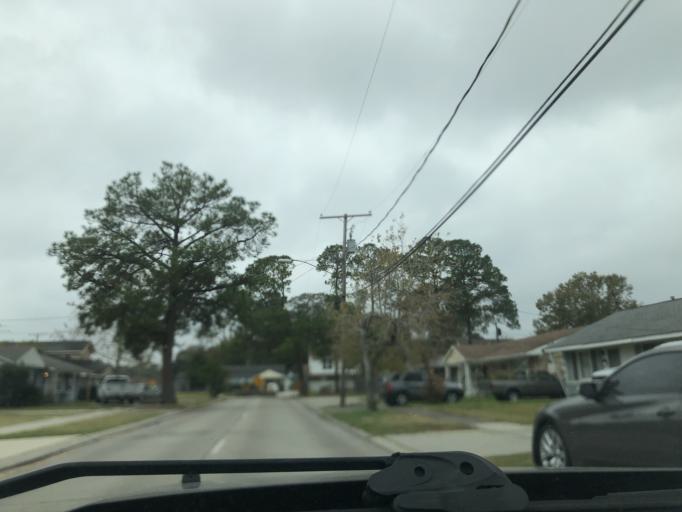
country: US
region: Louisiana
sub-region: Jefferson Parish
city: Metairie Terrace
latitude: 29.9822
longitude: -90.1635
